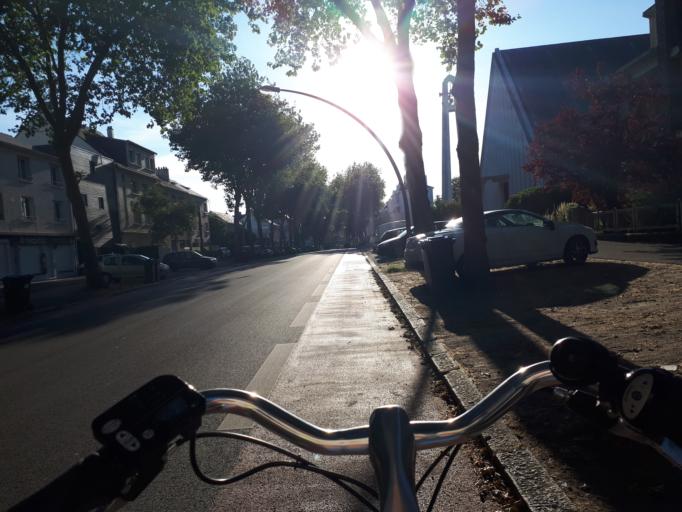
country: FR
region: Pays de la Loire
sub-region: Departement de la Loire-Atlantique
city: Saint-Nazaire
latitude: 47.2832
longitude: -2.2121
